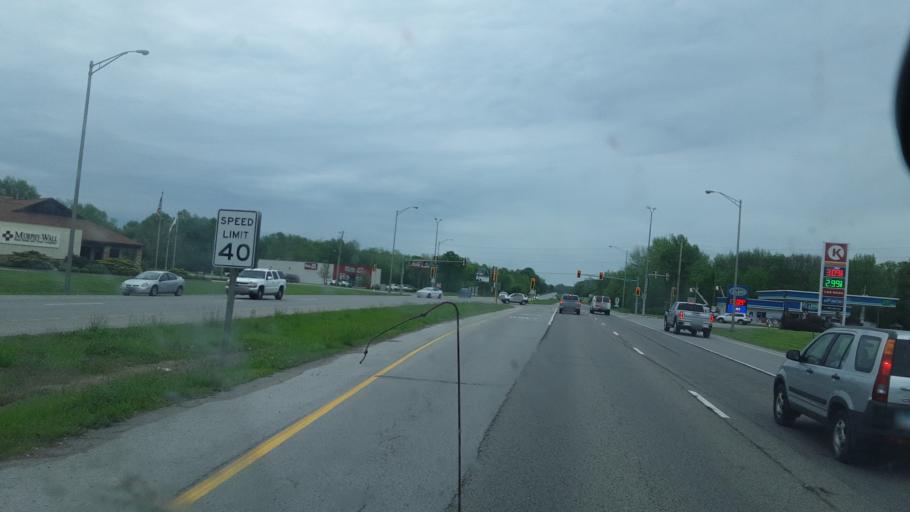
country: US
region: Illinois
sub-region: Jackson County
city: Murphysboro
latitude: 37.7651
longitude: -89.3186
